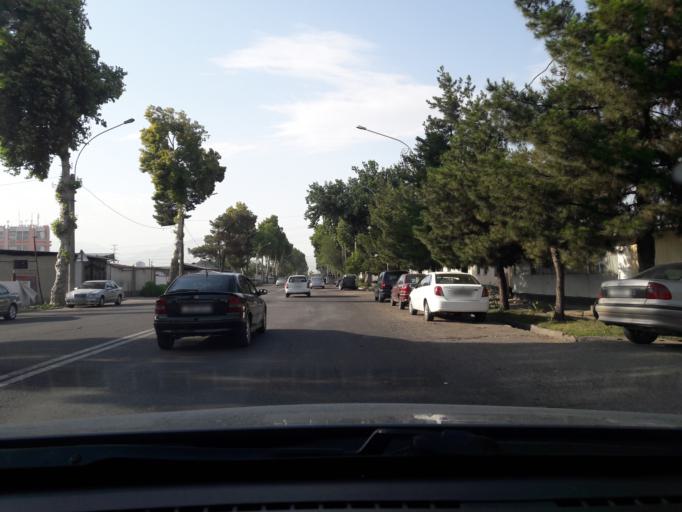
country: TJ
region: Dushanbe
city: Dushanbe
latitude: 38.5535
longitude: 68.7725
